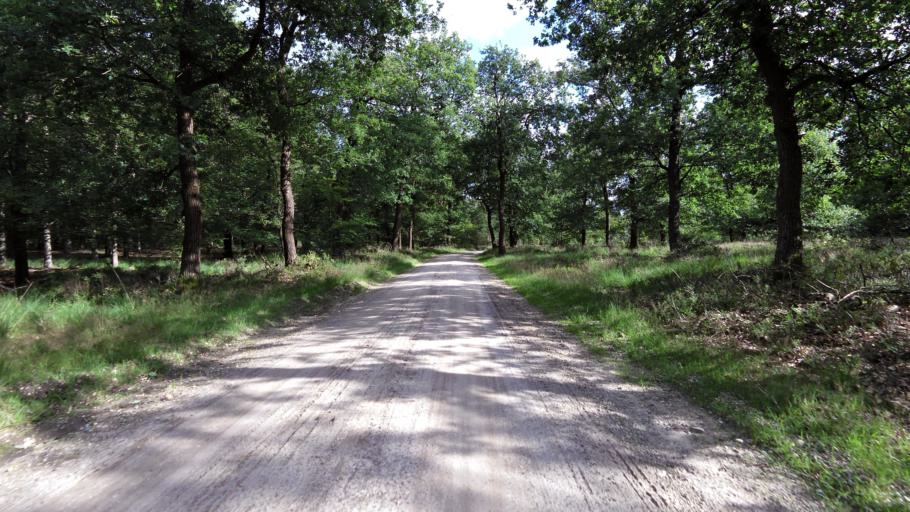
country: NL
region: Gelderland
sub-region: Gemeente Apeldoorn
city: Uddel
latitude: 52.2750
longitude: 5.8687
